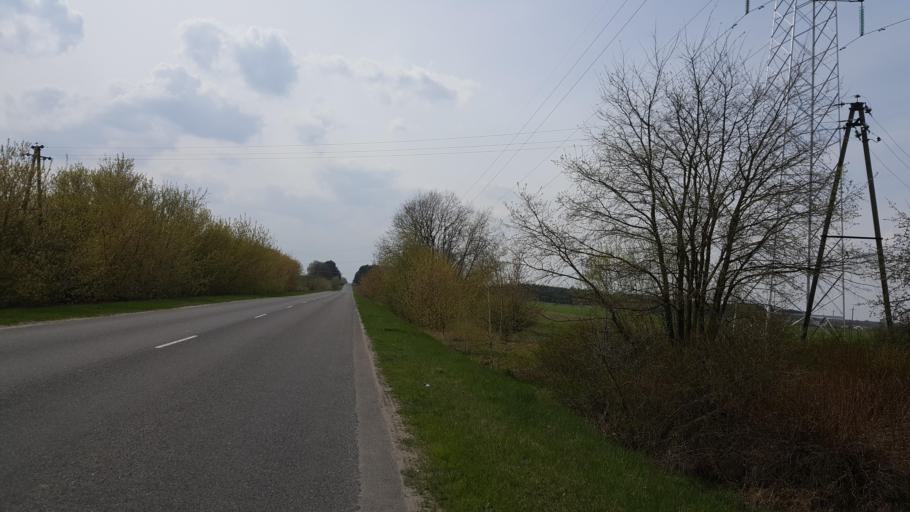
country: BY
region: Brest
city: Zhabinka
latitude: 52.2090
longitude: 23.9397
